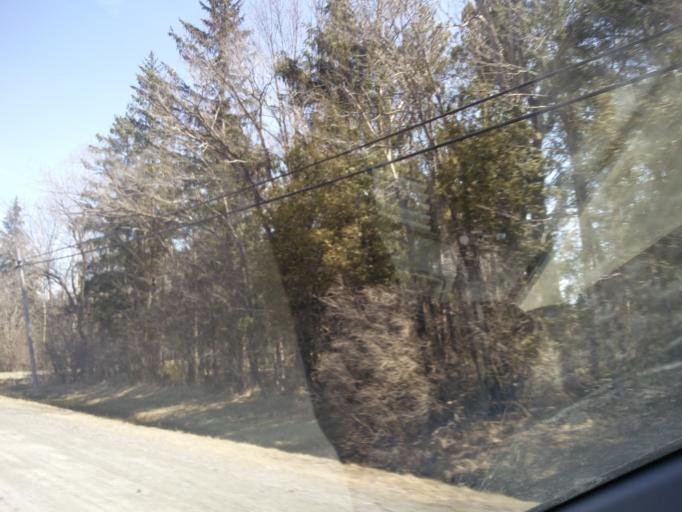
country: CA
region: Ontario
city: Bells Corners
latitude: 45.1822
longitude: -75.6382
